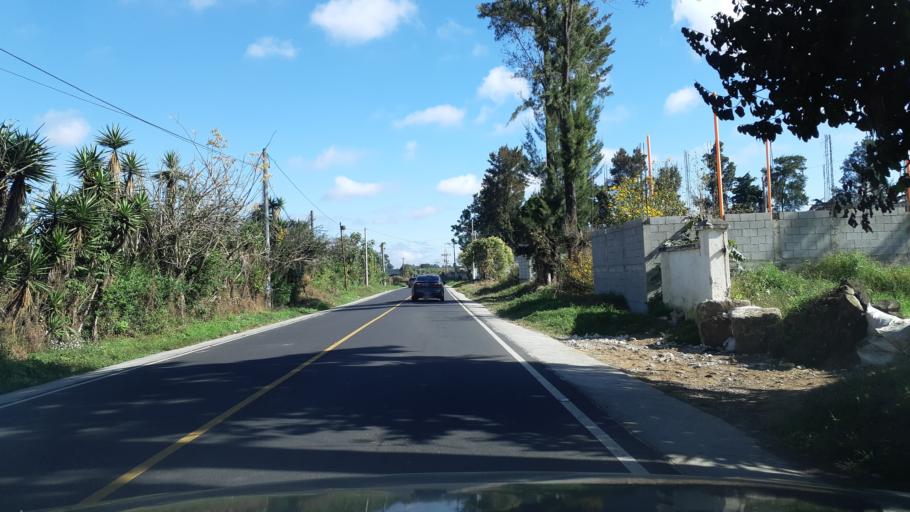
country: GT
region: Chimaltenango
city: San Andres Itzapa
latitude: 14.6357
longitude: -90.8266
